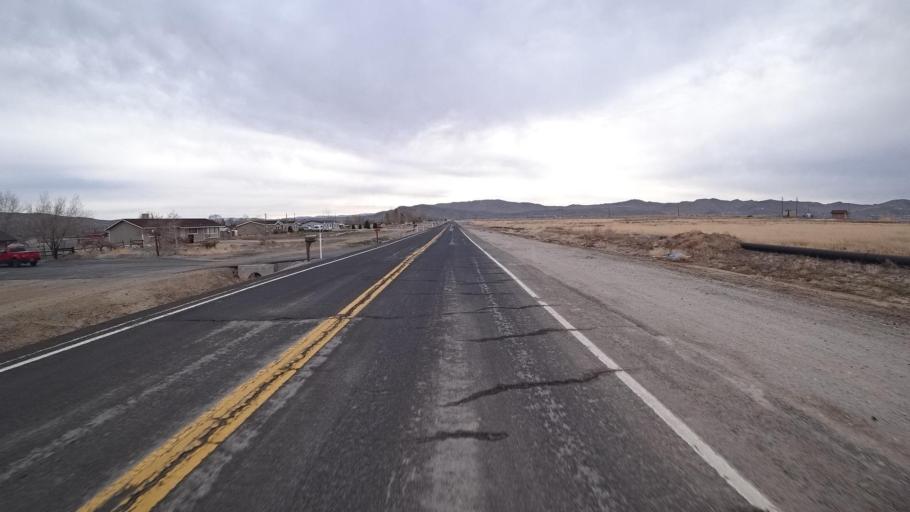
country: US
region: Nevada
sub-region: Washoe County
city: Lemmon Valley
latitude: 39.6745
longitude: -119.8450
